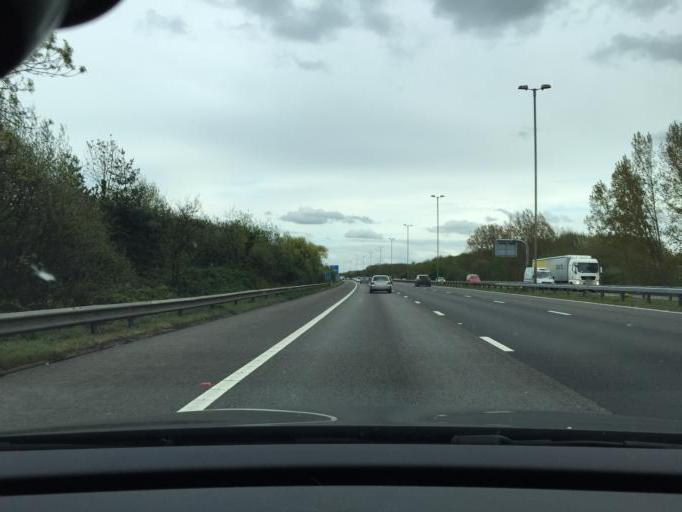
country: GB
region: England
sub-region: West Berkshire
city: Calcot
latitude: 51.4308
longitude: -1.0482
